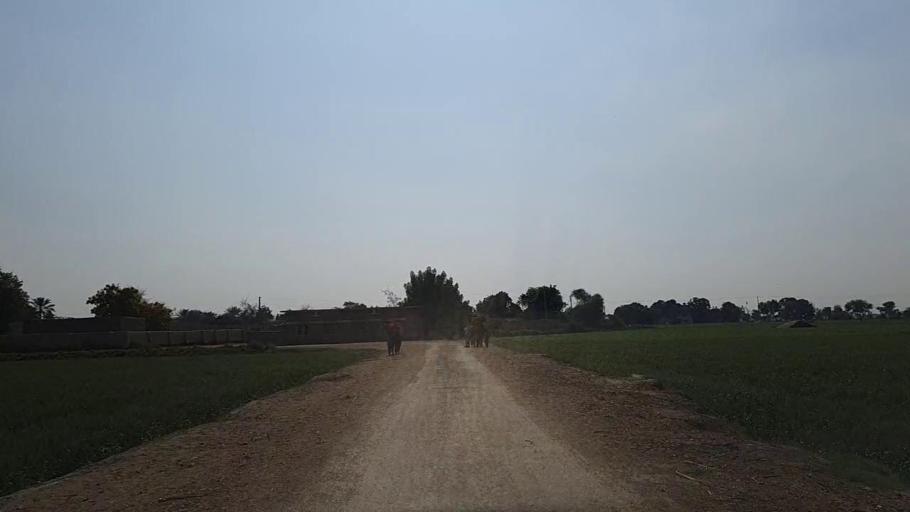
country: PK
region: Sindh
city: Nawabshah
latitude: 26.2511
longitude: 68.4920
